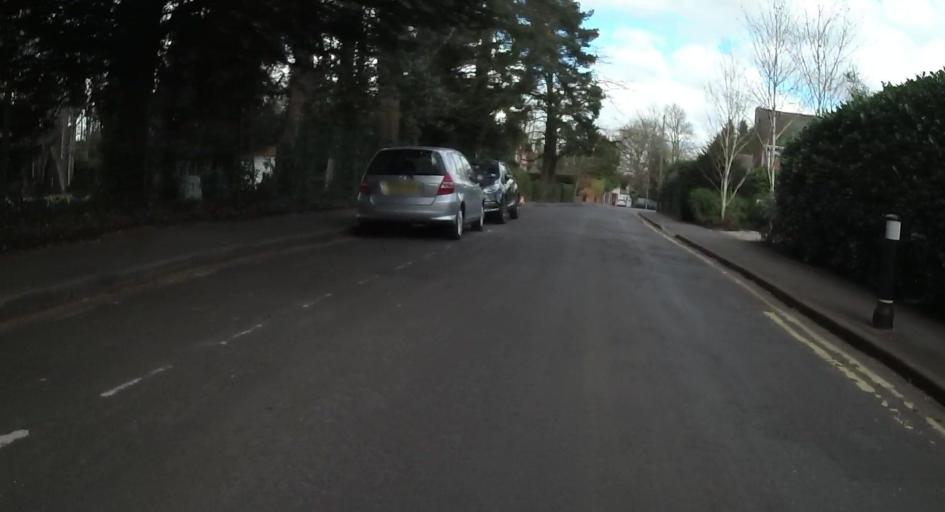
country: GB
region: England
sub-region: Surrey
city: Woking
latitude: 51.3202
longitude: -0.5470
